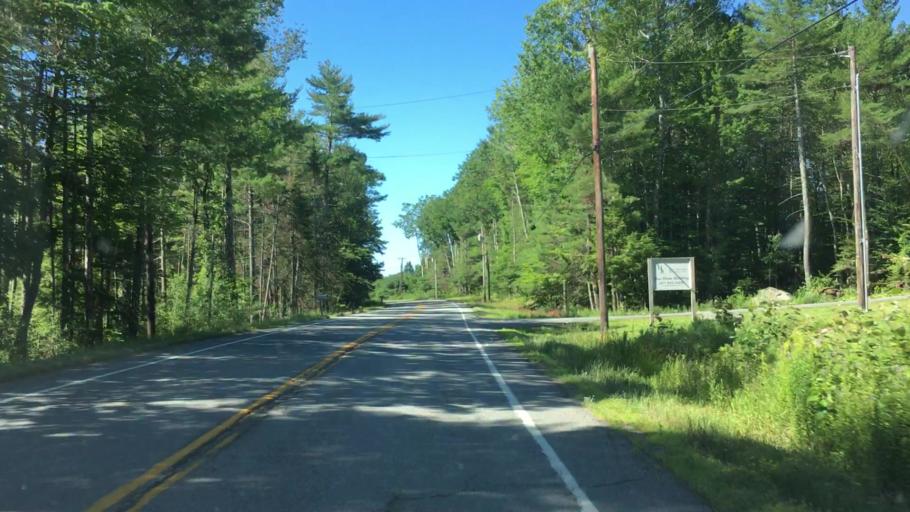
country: US
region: Maine
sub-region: Hancock County
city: Dedham
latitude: 44.6756
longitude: -68.6705
